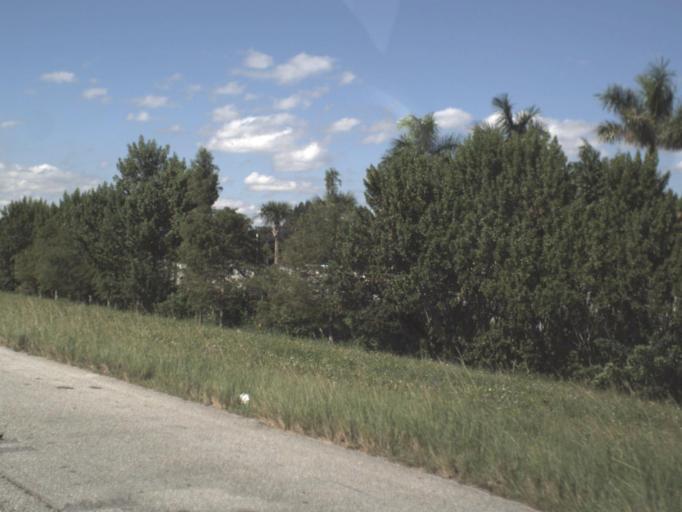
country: US
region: Florida
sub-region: Miami-Dade County
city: Country Club
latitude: 25.9675
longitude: -80.3287
